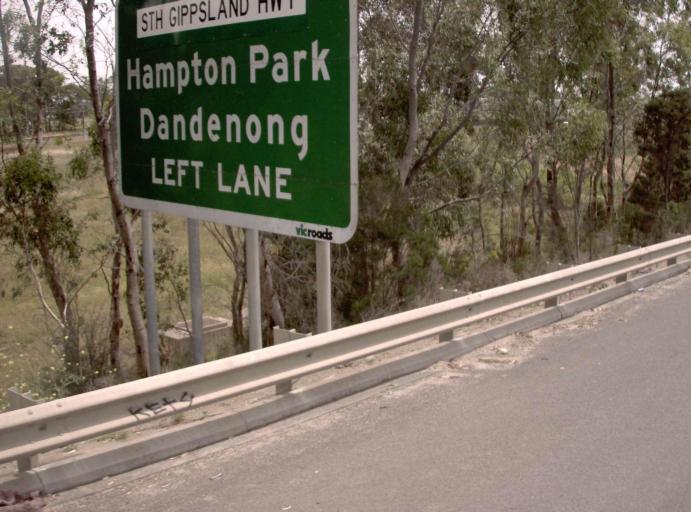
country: AU
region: Victoria
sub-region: Casey
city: Hampton Park
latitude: -38.0467
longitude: 145.2453
